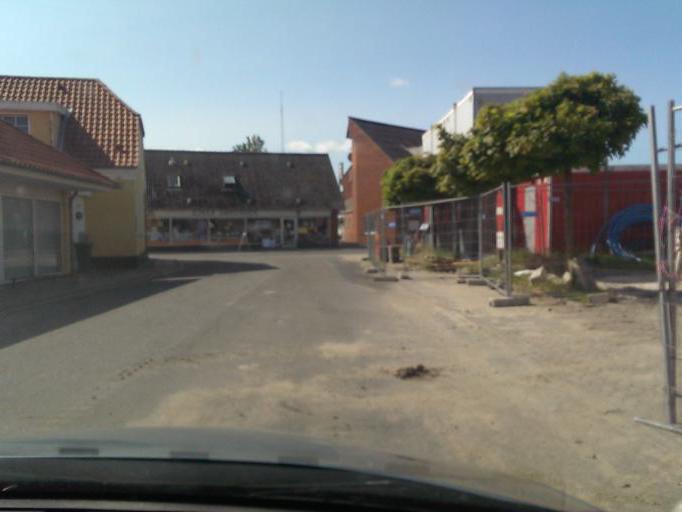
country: DK
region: North Denmark
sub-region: Jammerbugt Kommune
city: Abybro
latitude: 57.1631
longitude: 9.7308
